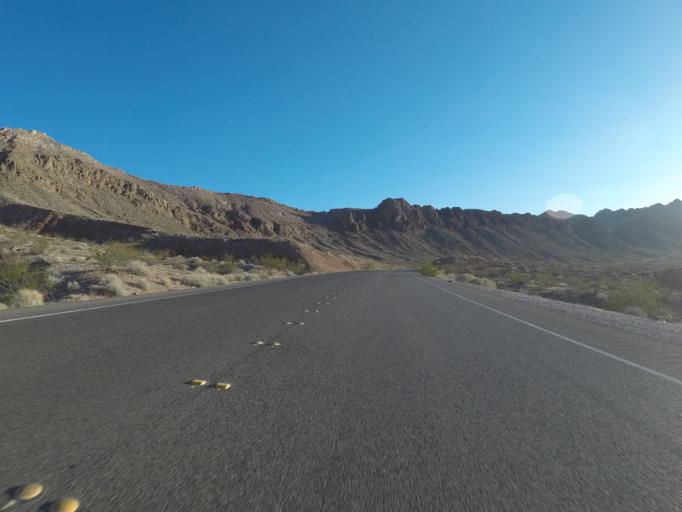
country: US
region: Nevada
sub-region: Clark County
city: Moapa Valley
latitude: 36.2562
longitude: -114.4820
